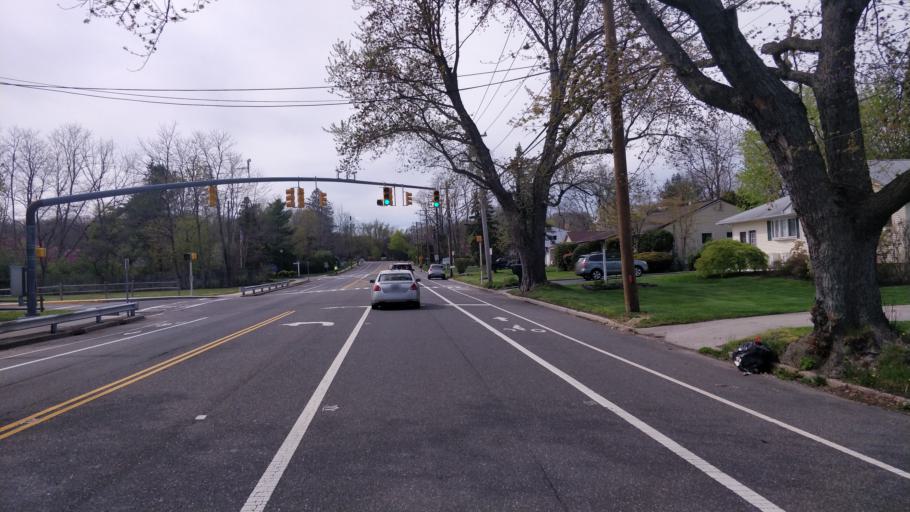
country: US
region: New York
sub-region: Suffolk County
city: Terryville
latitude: 40.9178
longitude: -73.0743
